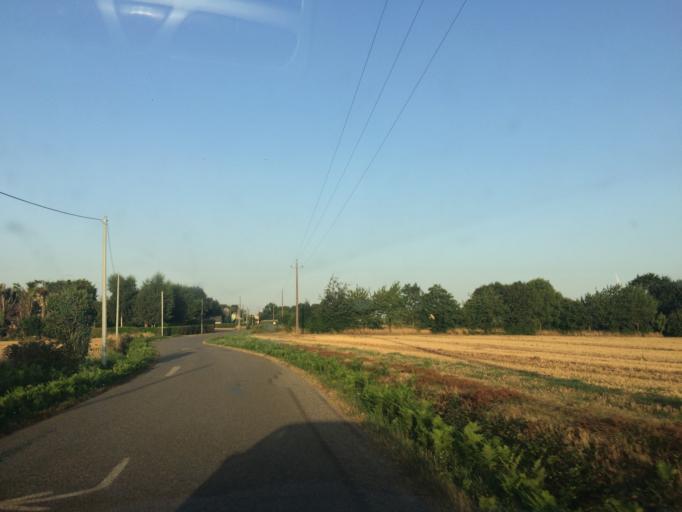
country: FR
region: Brittany
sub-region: Departement du Morbihan
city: Beganne
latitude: 47.6364
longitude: -2.2455
